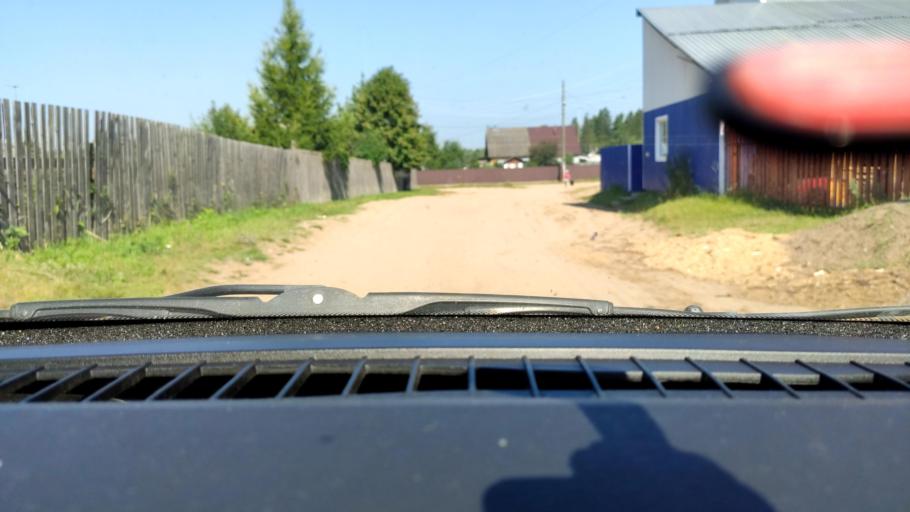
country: RU
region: Perm
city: Ust'-Kachka
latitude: 57.9323
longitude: 55.5163
